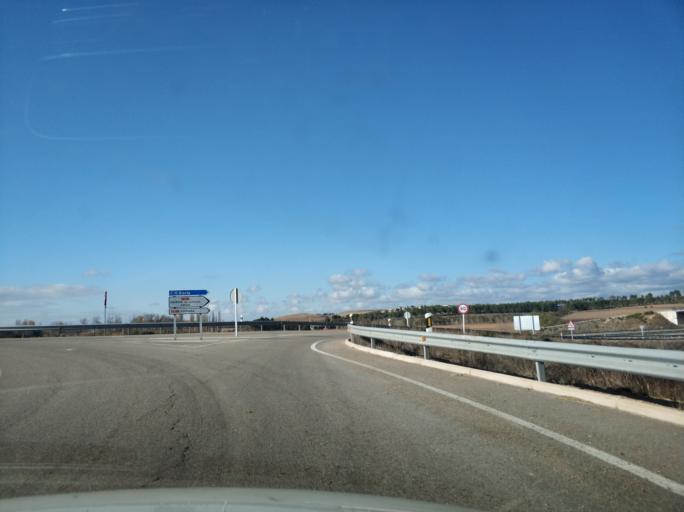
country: ES
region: Castille and Leon
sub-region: Provincia de Soria
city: Almazan
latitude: 41.4709
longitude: -2.5229
